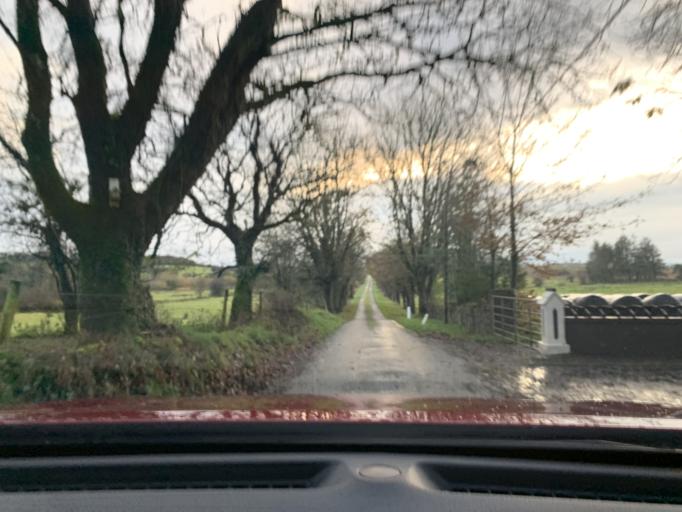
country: IE
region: Connaught
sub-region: Sligo
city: Ballymote
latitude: 54.0340
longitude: -8.5356
